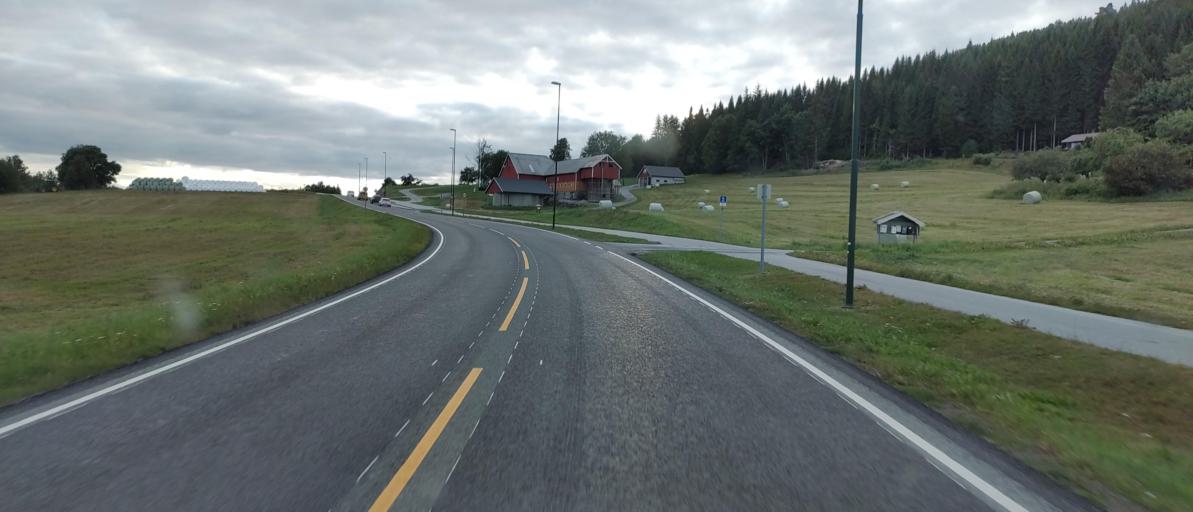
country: NO
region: More og Romsdal
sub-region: Molde
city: Hjelset
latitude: 62.7336
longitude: 7.4183
